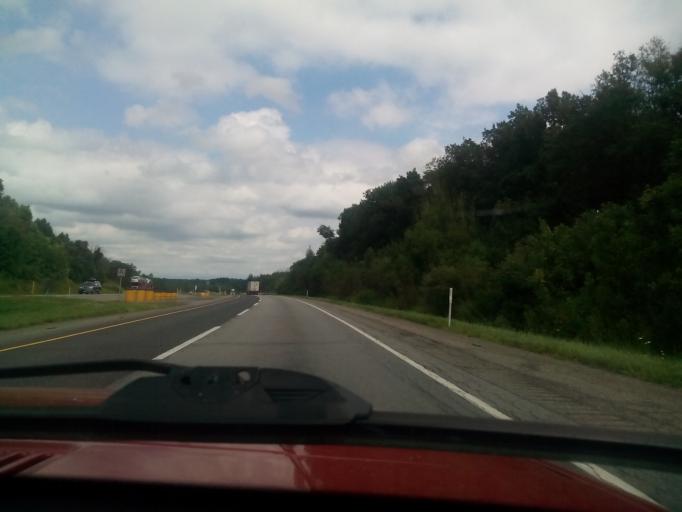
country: US
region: Indiana
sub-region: LaPorte County
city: Westville
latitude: 41.5975
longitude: -86.8672
